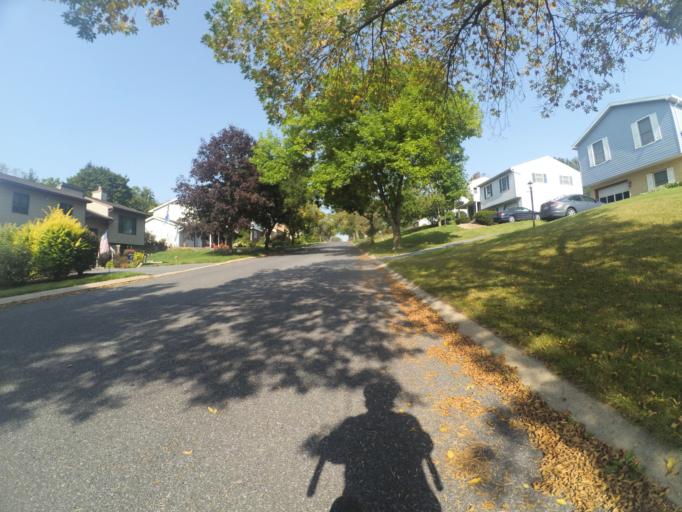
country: US
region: Pennsylvania
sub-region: Centre County
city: Lemont
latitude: 40.8045
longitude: -77.8136
